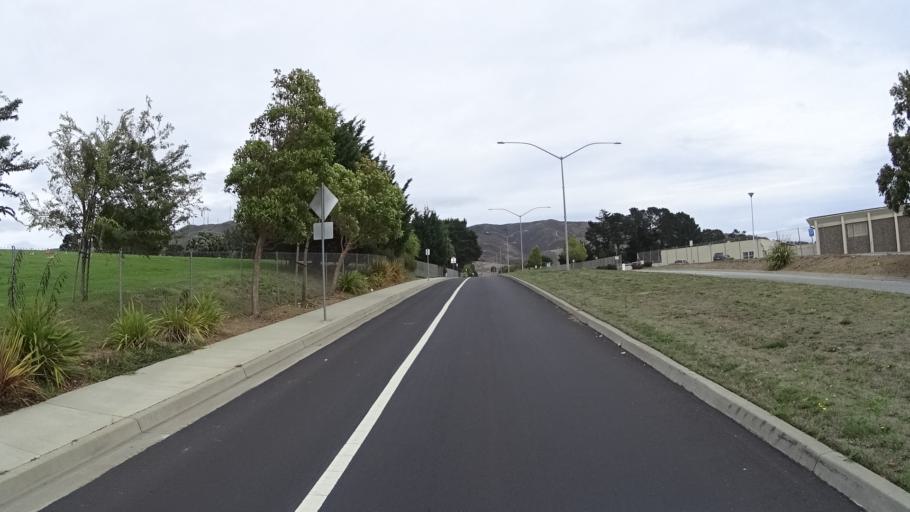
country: US
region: California
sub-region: San Mateo County
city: Colma
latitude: 37.6668
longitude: -122.4432
